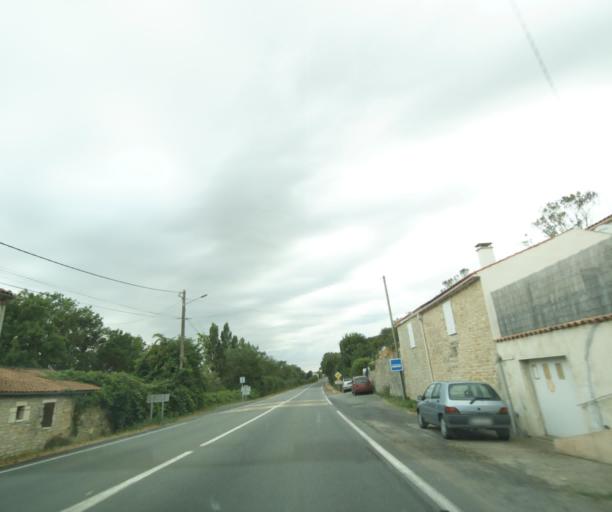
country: FR
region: Pays de la Loire
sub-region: Departement de la Vendee
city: Chaille-les-Marais
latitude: 46.3975
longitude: -1.0287
